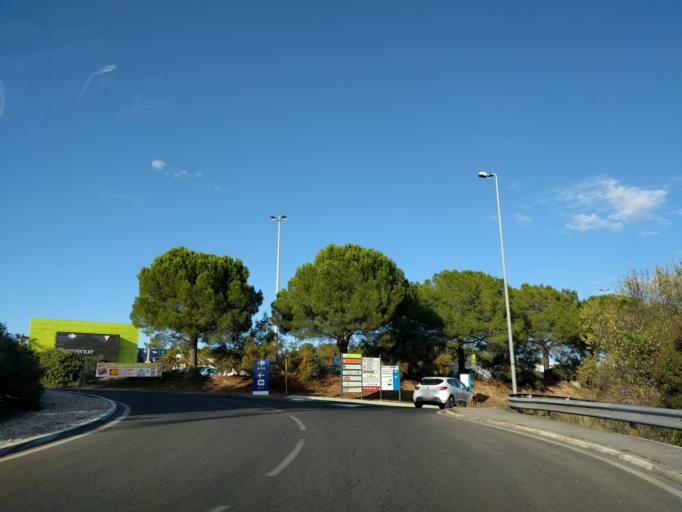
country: FR
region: Languedoc-Roussillon
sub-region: Departement de l'Herault
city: Montferrier-sur-Lez
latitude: 43.6479
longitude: 3.8425
